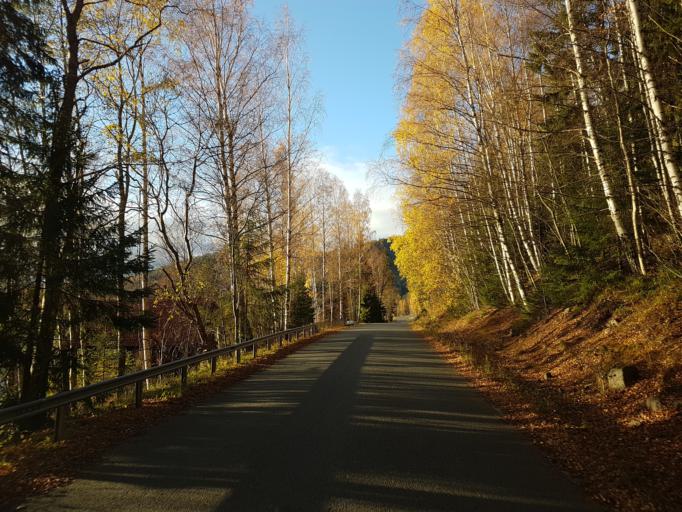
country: SE
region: Vaesternorrland
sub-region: Kramfors Kommun
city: Nordingra
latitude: 63.0648
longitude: 18.3755
